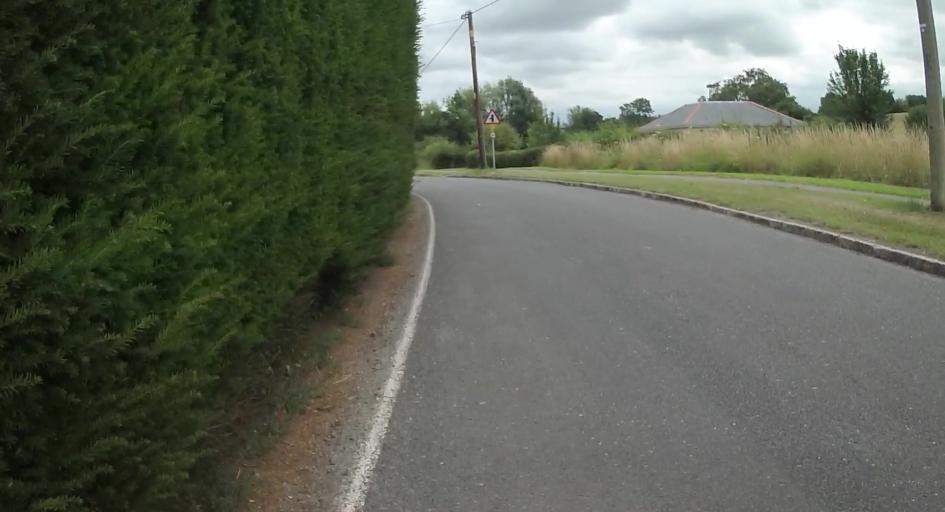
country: GB
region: England
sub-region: Hampshire
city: Swanmore
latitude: 51.0504
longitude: -1.1651
